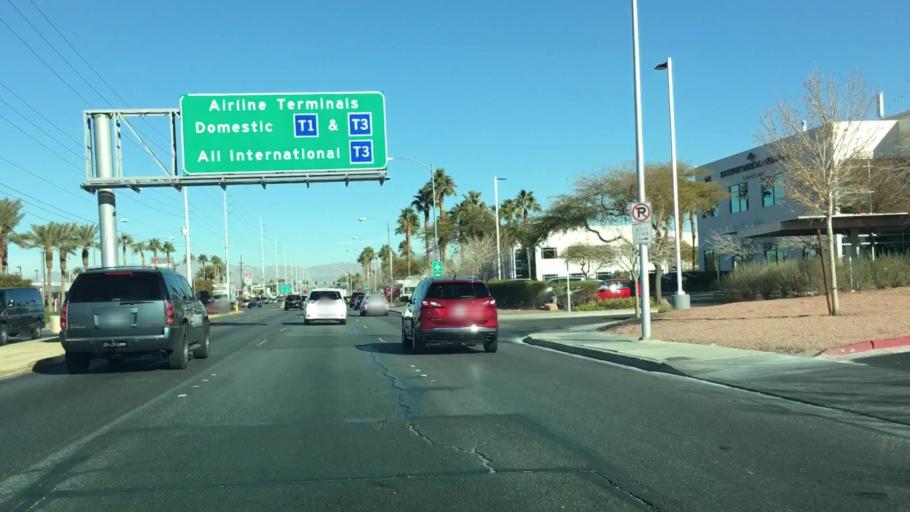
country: US
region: Nevada
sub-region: Clark County
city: Paradise
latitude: 36.0833
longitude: -115.1187
